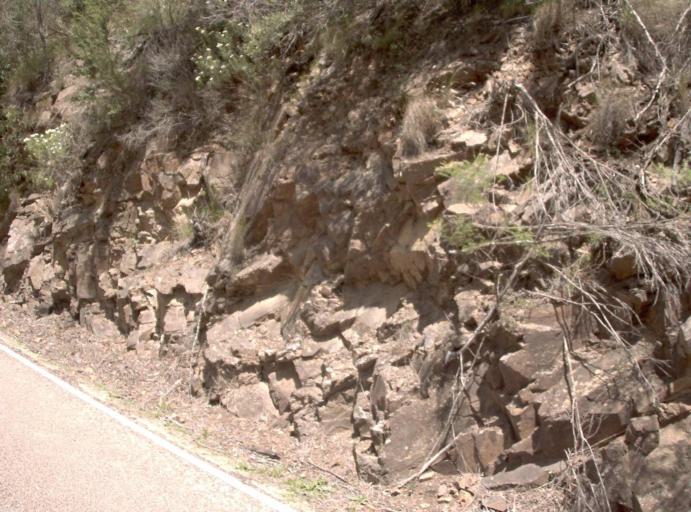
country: AU
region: Victoria
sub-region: East Gippsland
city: Lakes Entrance
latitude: -37.5379
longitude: 147.8641
